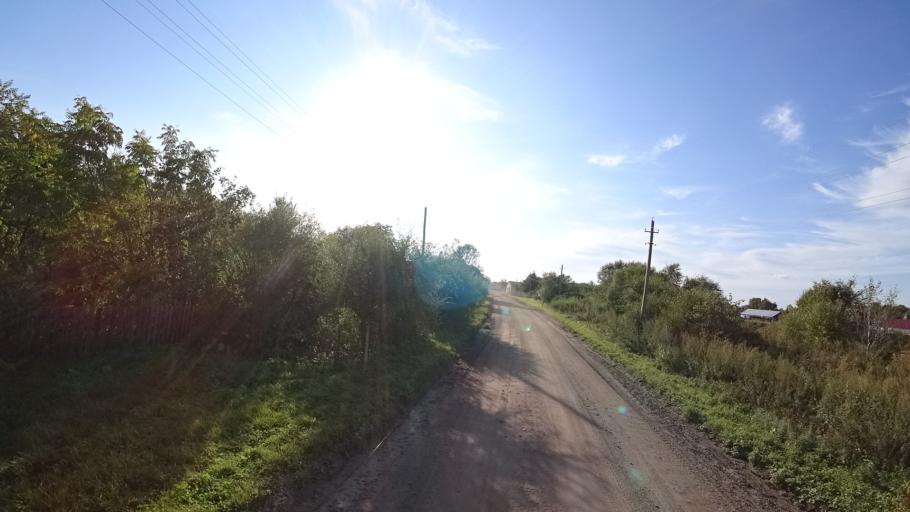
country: RU
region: Amur
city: Arkhara
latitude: 49.3571
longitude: 130.1192
